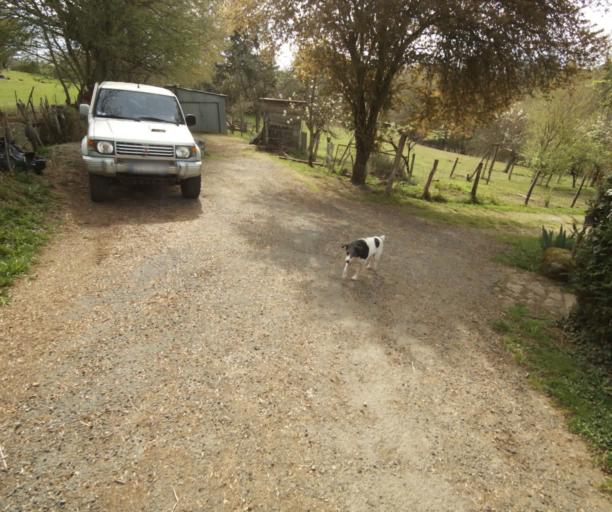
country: FR
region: Limousin
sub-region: Departement de la Correze
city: Correze
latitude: 45.3929
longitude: 1.8071
